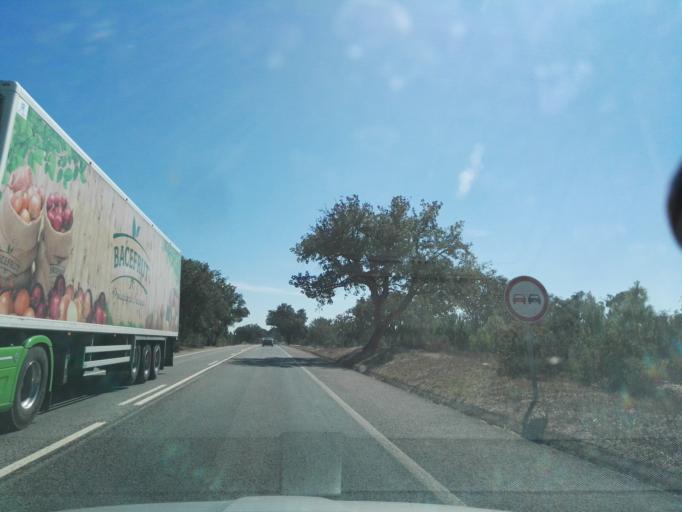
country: PT
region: Santarem
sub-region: Benavente
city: Poceirao
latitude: 38.8786
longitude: -8.8117
